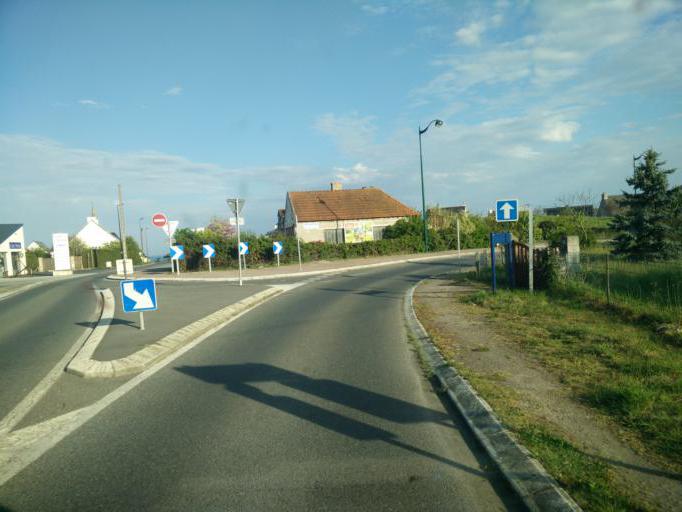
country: FR
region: Brittany
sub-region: Departement des Cotes-d'Armor
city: Erquy
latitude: 48.6271
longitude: -2.4543
